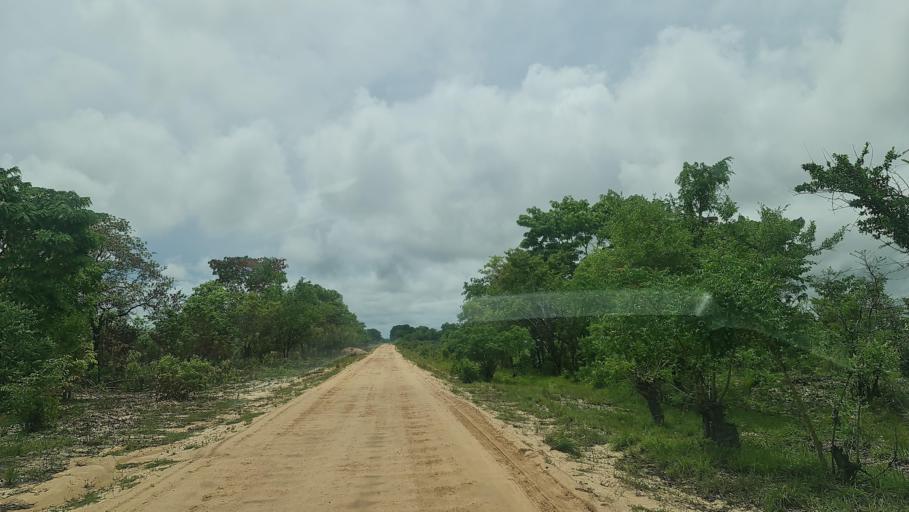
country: MZ
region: Zambezia
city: Quelimane
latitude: -17.2582
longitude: 37.2294
